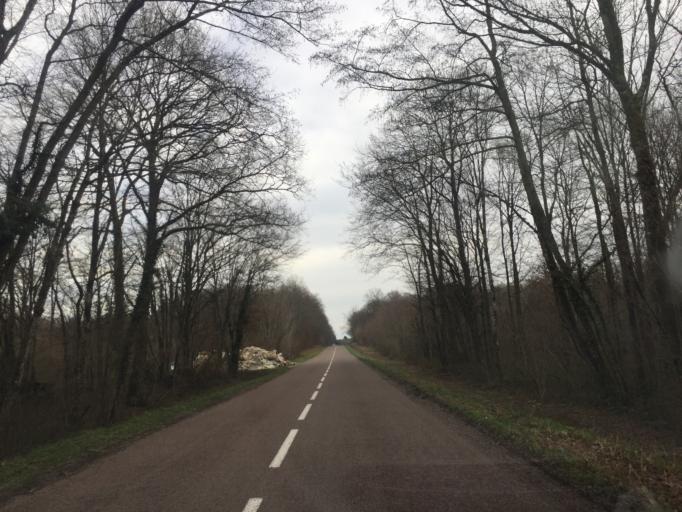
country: FR
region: Franche-Comte
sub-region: Departement du Jura
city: Chaussin
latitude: 46.9220
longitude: 5.4958
